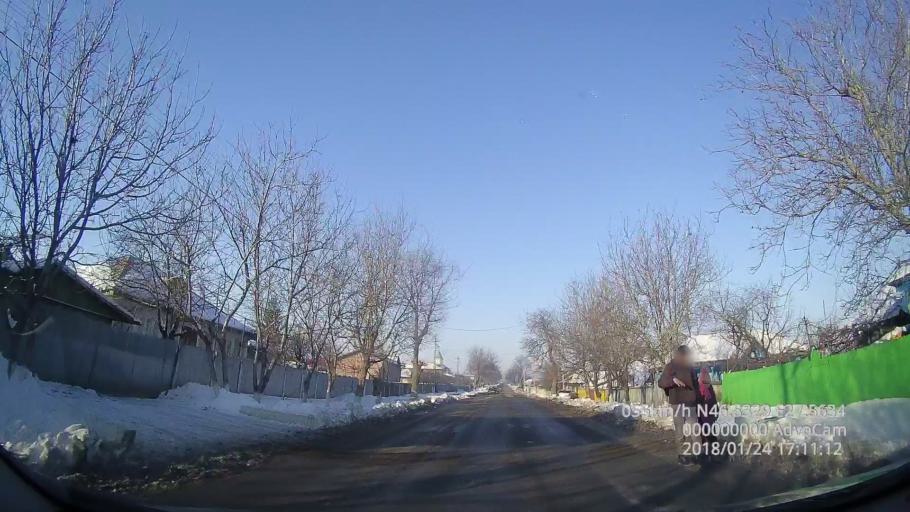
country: RO
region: Vaslui
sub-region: Comuna Vulturesti
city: Vulturesti
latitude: 46.8333
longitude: 27.5633
